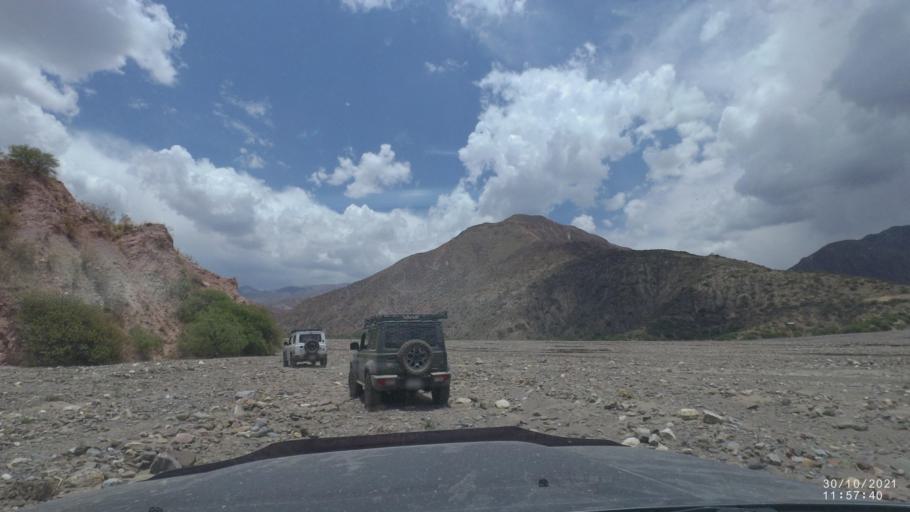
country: BO
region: Cochabamba
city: Colchani
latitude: -17.5233
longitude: -66.6180
